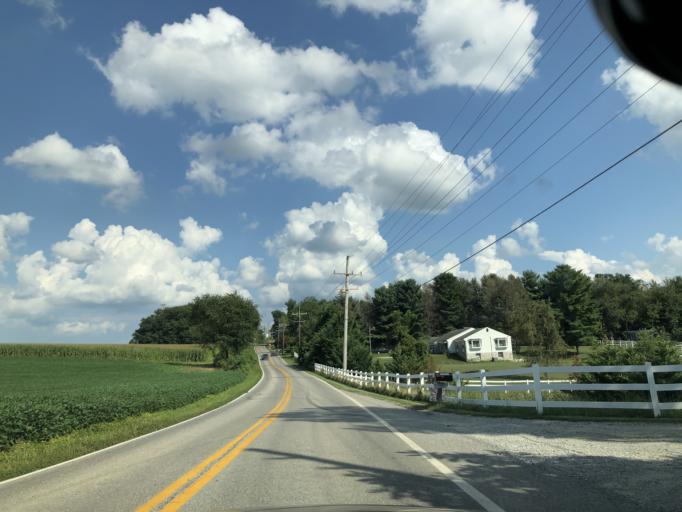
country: US
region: Maryland
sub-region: Carroll County
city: Mount Airy
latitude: 39.3972
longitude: -77.1880
